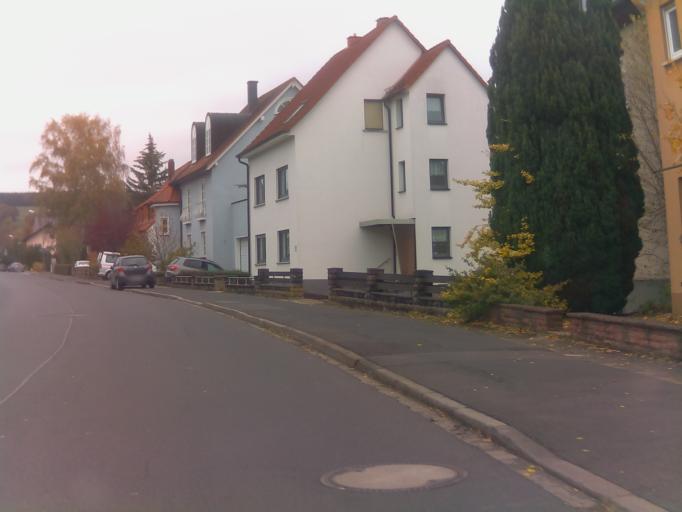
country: DE
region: Hesse
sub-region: Regierungsbezirk Kassel
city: Fulda
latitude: 50.5726
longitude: 9.6734
